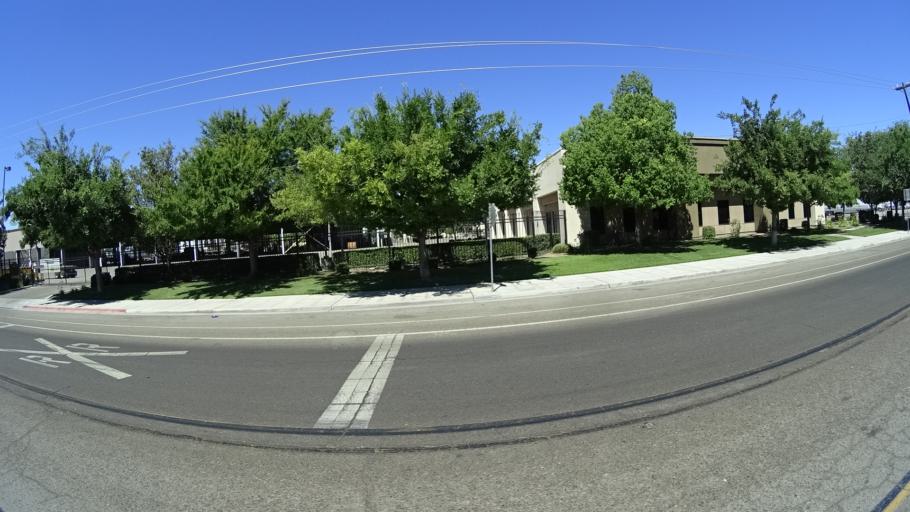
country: US
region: California
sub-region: Fresno County
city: Fresno
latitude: 36.6990
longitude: -119.7727
